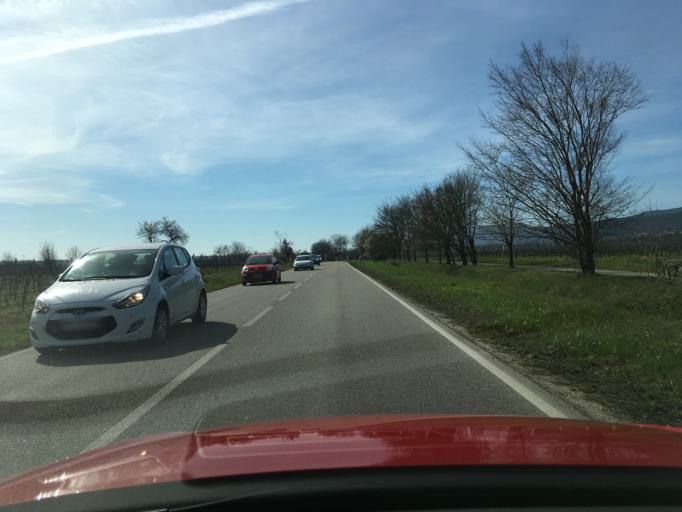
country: DE
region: Rheinland-Pfalz
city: Deidesheim
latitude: 49.3952
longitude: 8.1831
